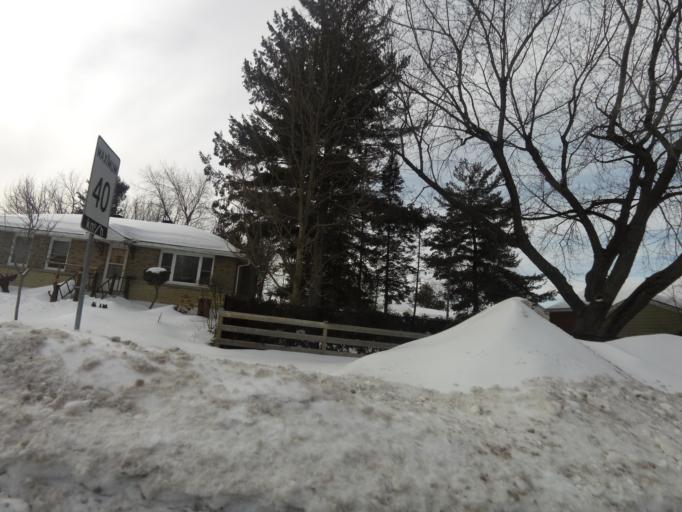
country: CA
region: Ontario
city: Ottawa
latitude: 45.4418
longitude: -75.6076
